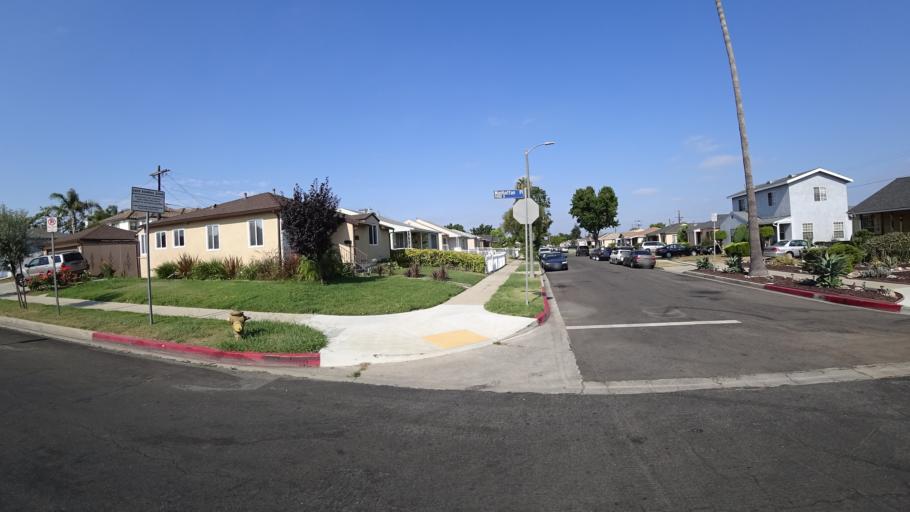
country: US
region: California
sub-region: Los Angeles County
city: Westmont
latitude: 33.9505
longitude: -118.3101
